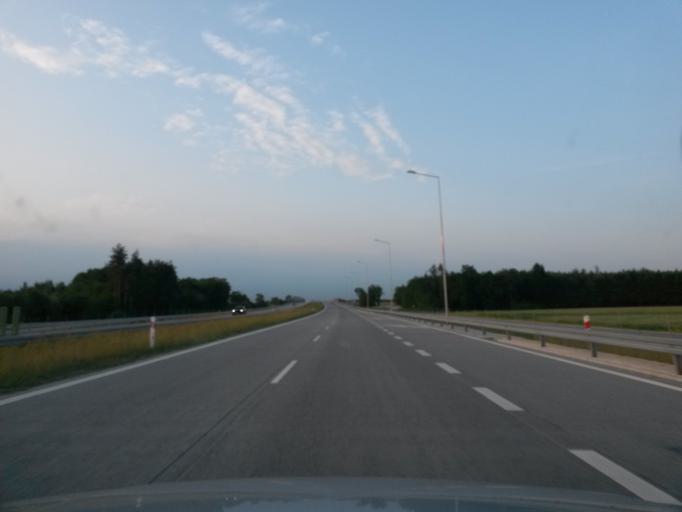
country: PL
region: Lodz Voivodeship
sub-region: Powiat wielunski
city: Czarnozyly
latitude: 51.3610
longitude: 18.5293
